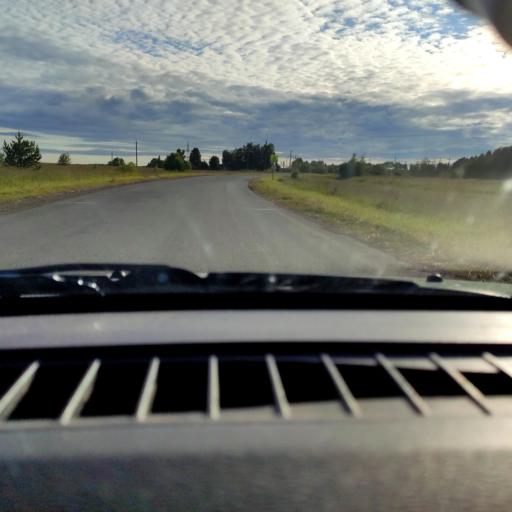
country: RU
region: Perm
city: Uinskoye
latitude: 57.0978
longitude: 56.6442
